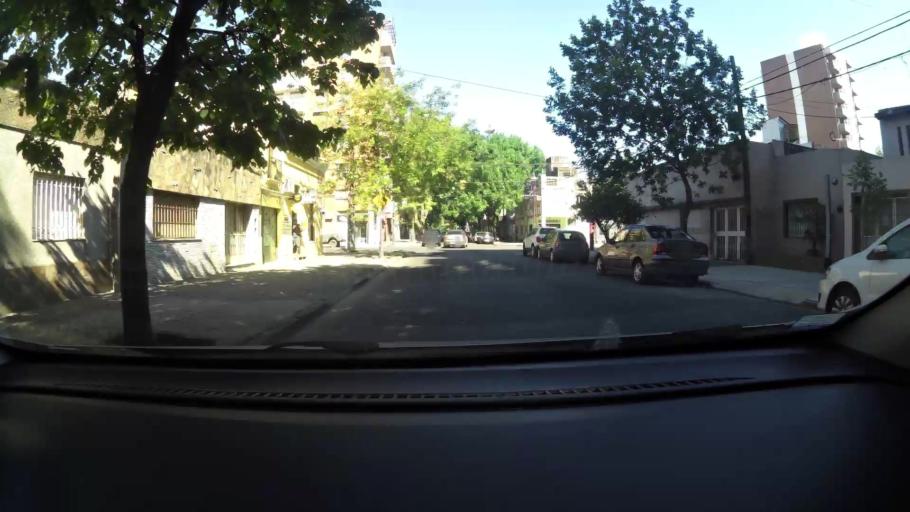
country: AR
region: Santa Fe
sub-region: Departamento de Rosario
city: Rosario
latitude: -32.9493
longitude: -60.6728
